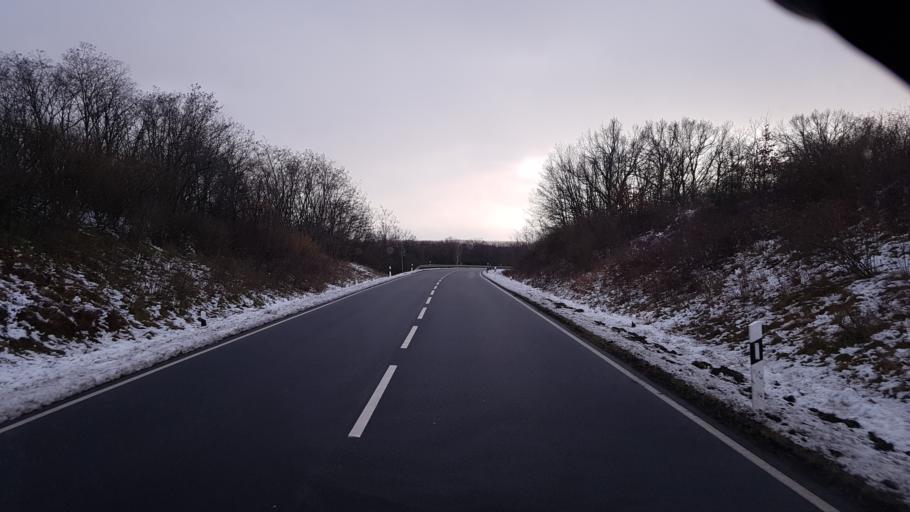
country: DE
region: Brandenburg
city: Heinersbruck
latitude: 51.8402
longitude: 14.5865
